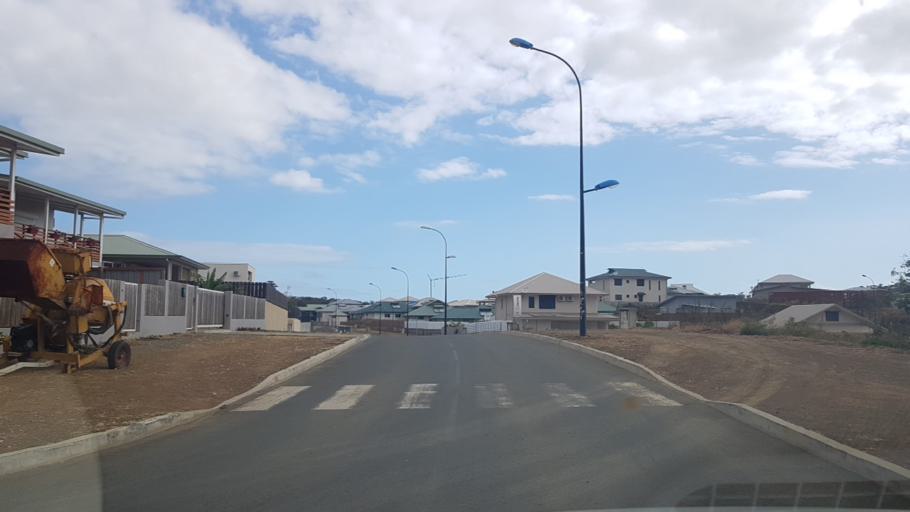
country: NC
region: South Province
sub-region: Dumbea
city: Dumbea
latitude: -22.1991
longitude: 166.4418
